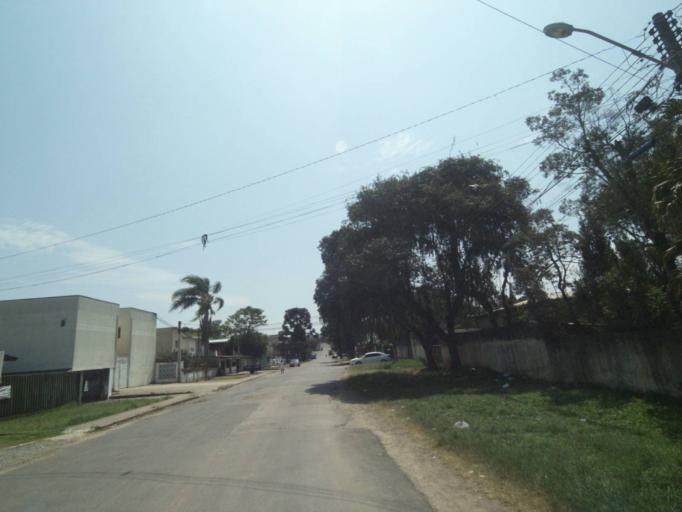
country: BR
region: Parana
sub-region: Curitiba
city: Curitiba
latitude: -25.4824
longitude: -49.3128
